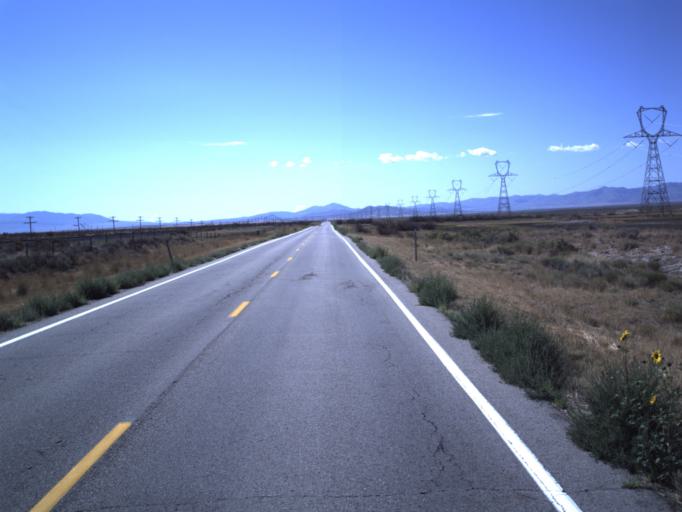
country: US
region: Utah
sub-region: Tooele County
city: Tooele
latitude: 40.3287
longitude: -112.4080
